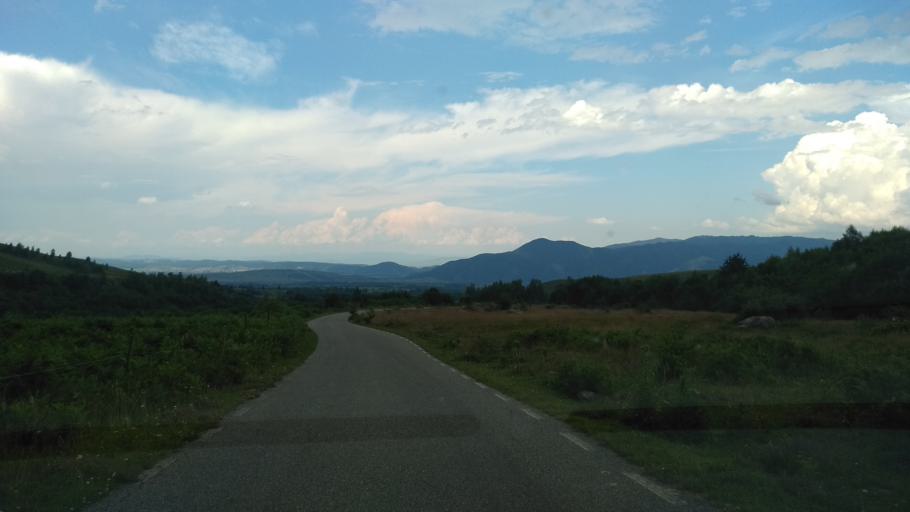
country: RO
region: Hunedoara
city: Salasu de Sus
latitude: 45.4783
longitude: 22.9631
